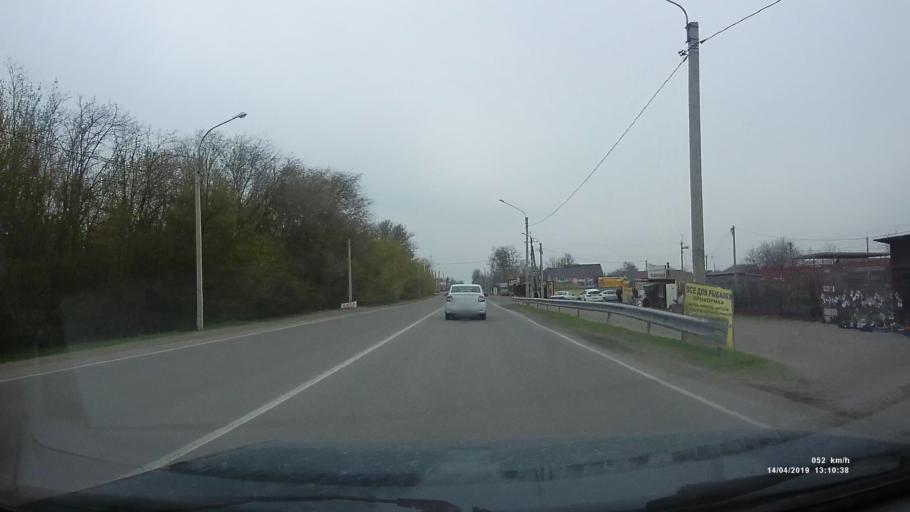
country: RU
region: Rostov
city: Kuleshovka
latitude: 47.1089
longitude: 39.6504
